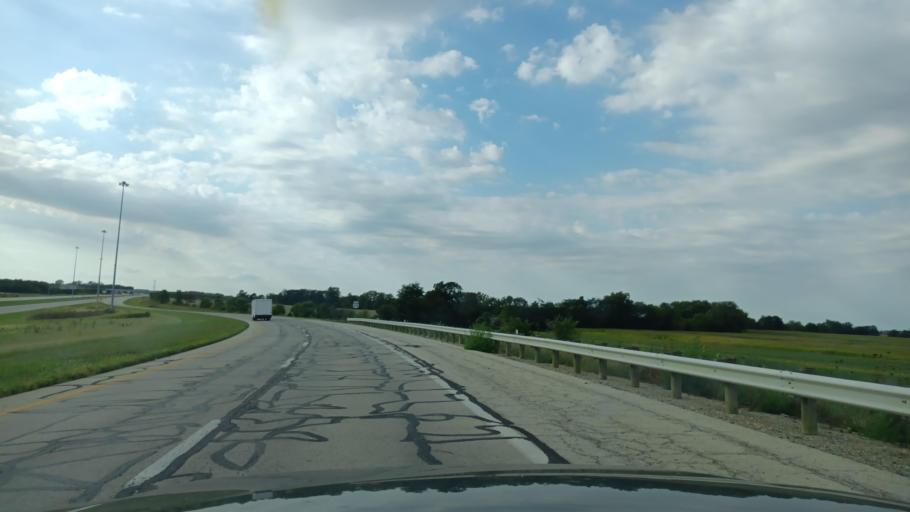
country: US
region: Ohio
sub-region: Fayette County
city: Jeffersonville
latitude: 39.6356
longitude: -83.6222
